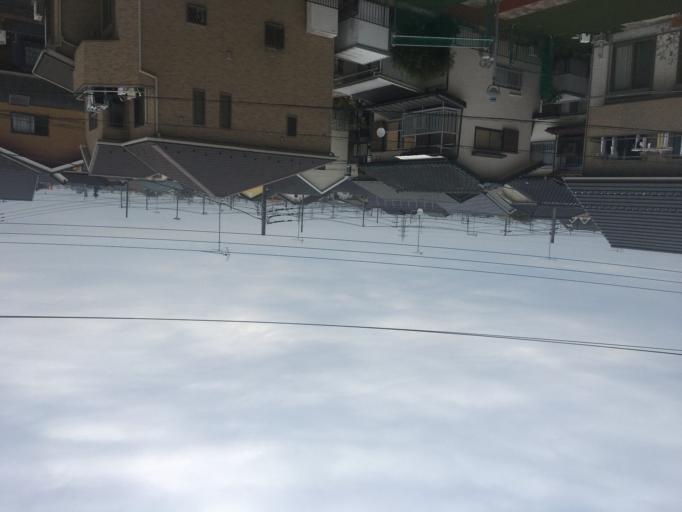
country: JP
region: Saitama
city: Hanno
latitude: 35.8438
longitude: 139.3328
